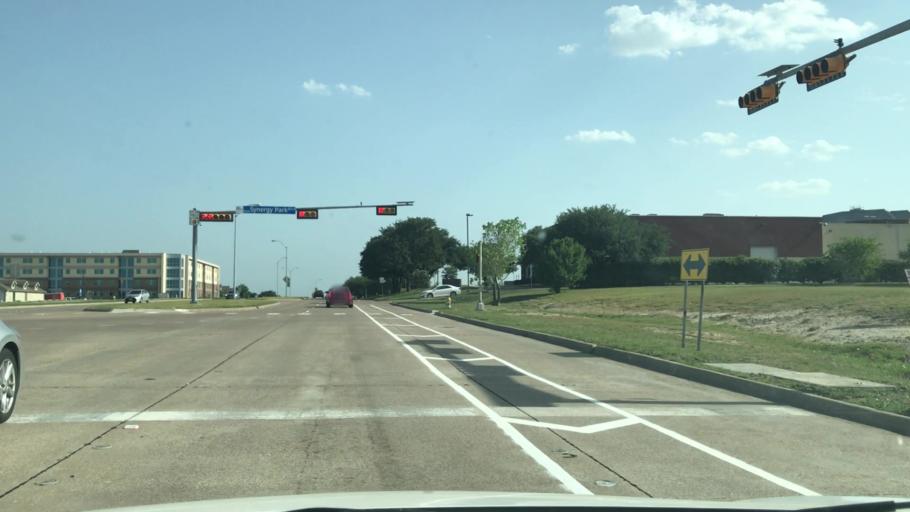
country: US
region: Texas
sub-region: Dallas County
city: Richardson
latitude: 32.9933
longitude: -96.7564
